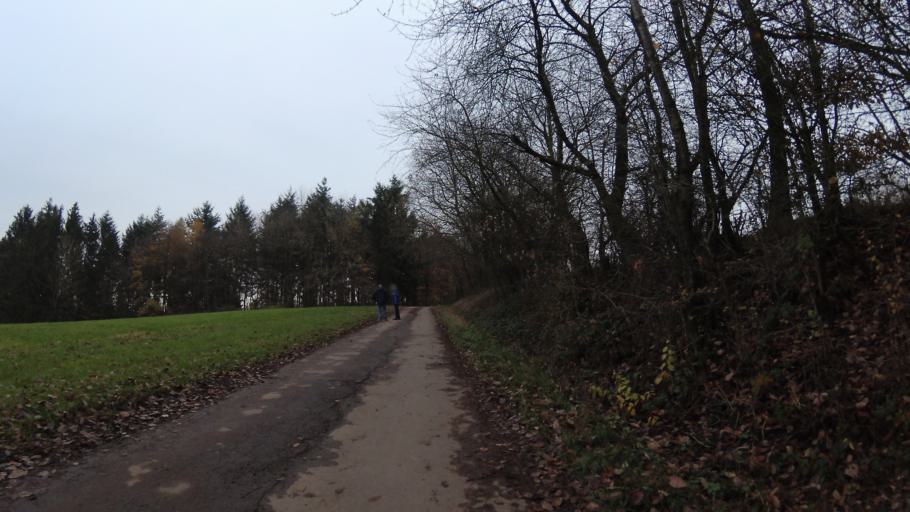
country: DE
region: Saarland
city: Marpingen
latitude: 49.4150
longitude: 7.0606
